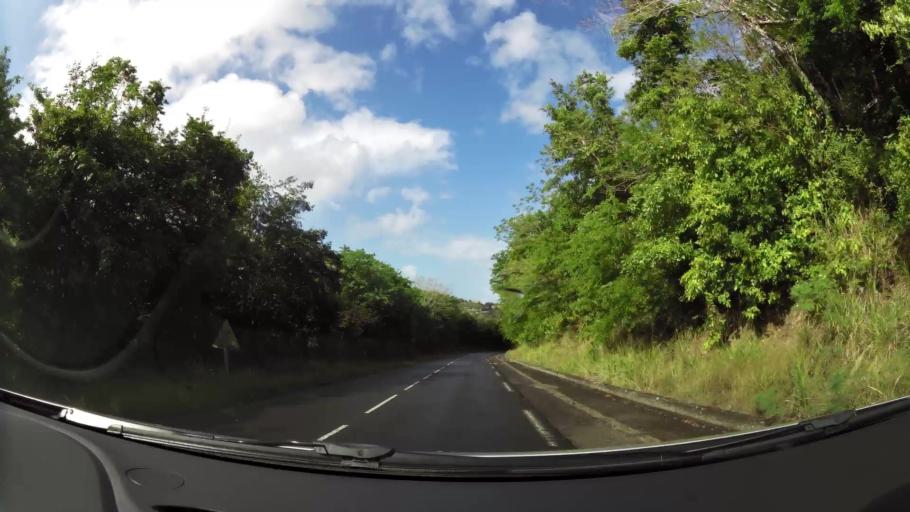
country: MQ
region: Martinique
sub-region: Martinique
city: Les Trois-Ilets
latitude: 14.5382
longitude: -61.0565
